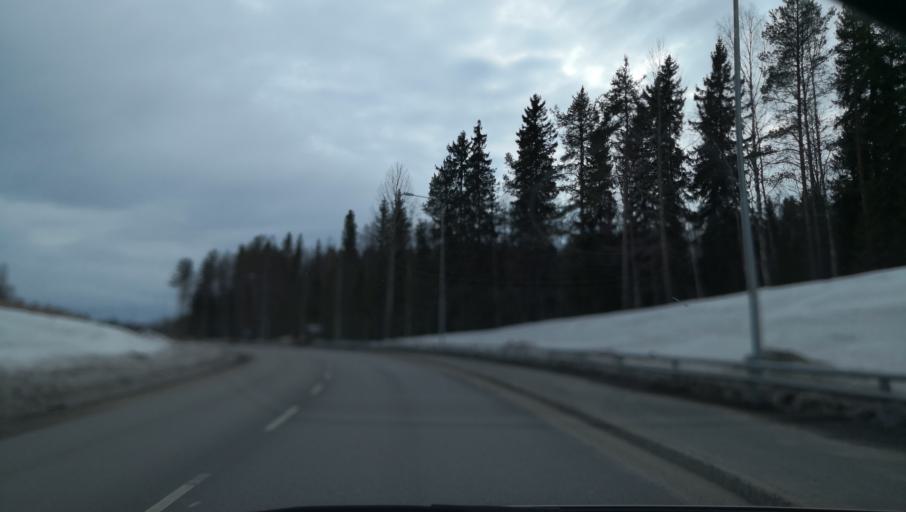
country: SE
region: Vaesterbotten
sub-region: Vannas Kommun
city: Vaennaes
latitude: 63.9125
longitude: 19.7697
